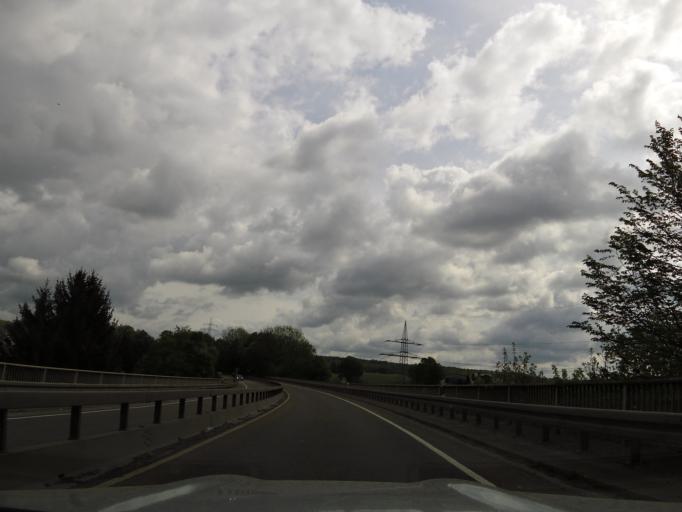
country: DE
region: Hesse
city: Merenberg
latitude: 50.4827
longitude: 8.1593
